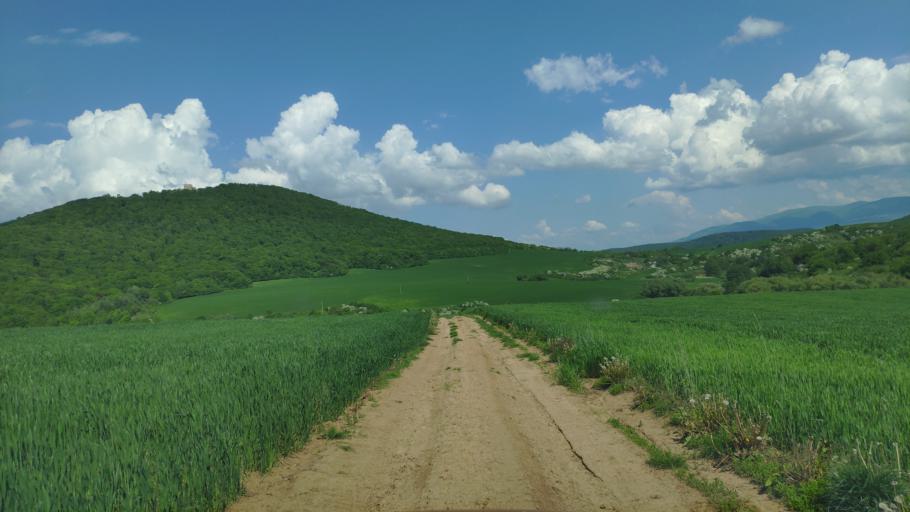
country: SK
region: Presovsky
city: Sabinov
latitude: 49.0461
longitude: 21.1573
